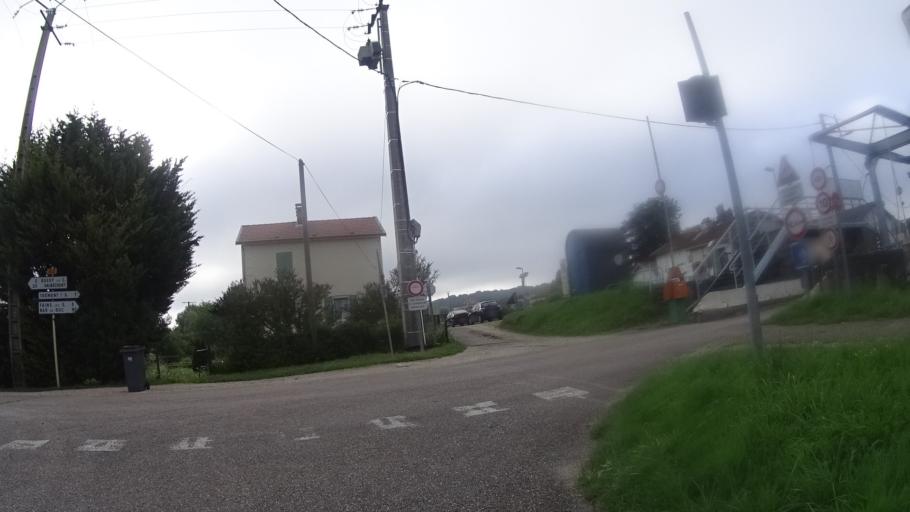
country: FR
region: Lorraine
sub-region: Departement de la Meuse
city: Fains-Veel
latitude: 48.8039
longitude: 5.0704
